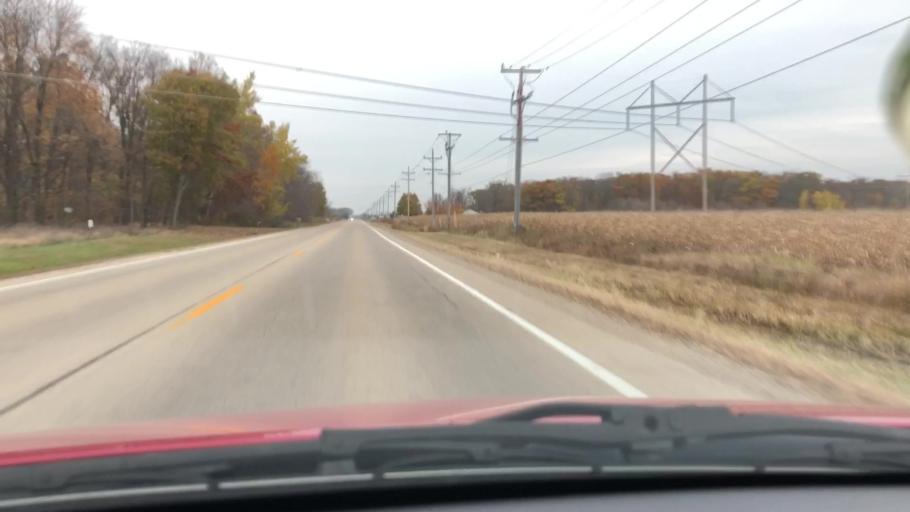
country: US
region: Wisconsin
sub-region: Outagamie County
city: Seymour
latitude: 44.4594
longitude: -88.2912
